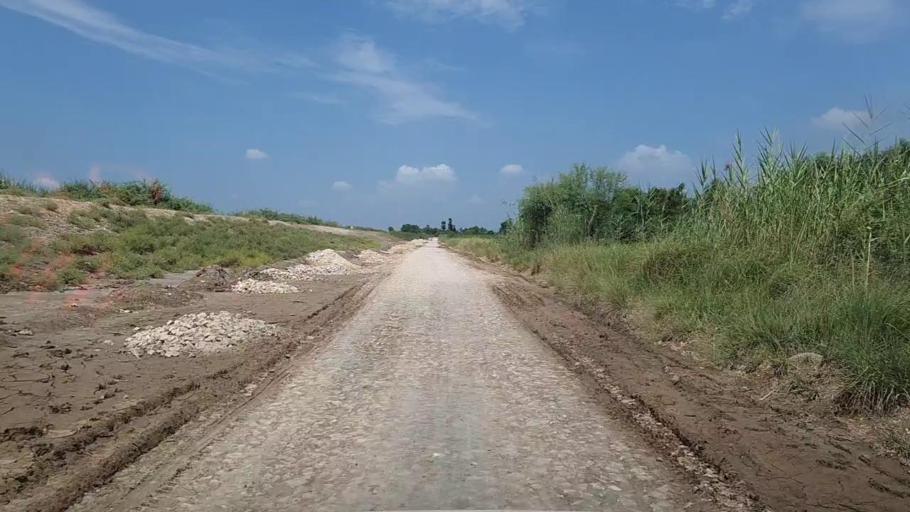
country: PK
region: Sindh
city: Bhiria
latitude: 26.9083
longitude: 68.2022
